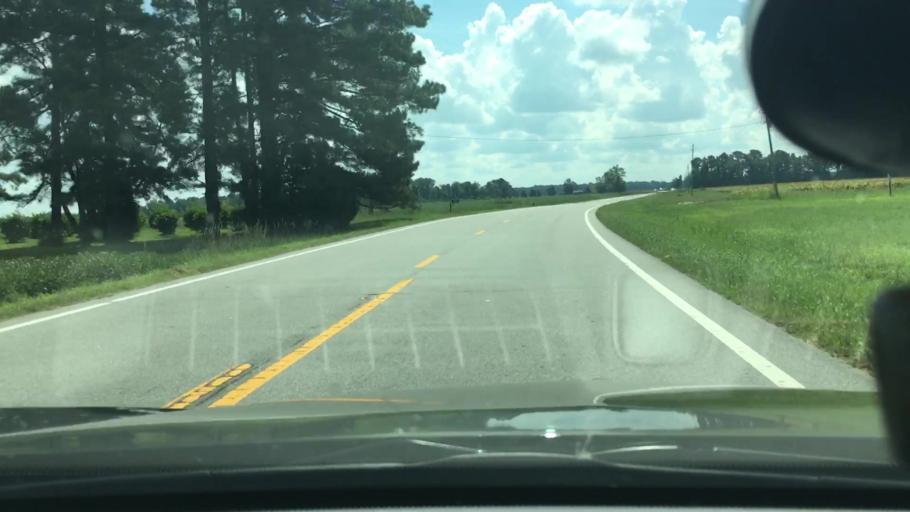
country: US
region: North Carolina
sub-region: Pitt County
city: Greenville
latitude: 35.6689
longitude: -77.4802
